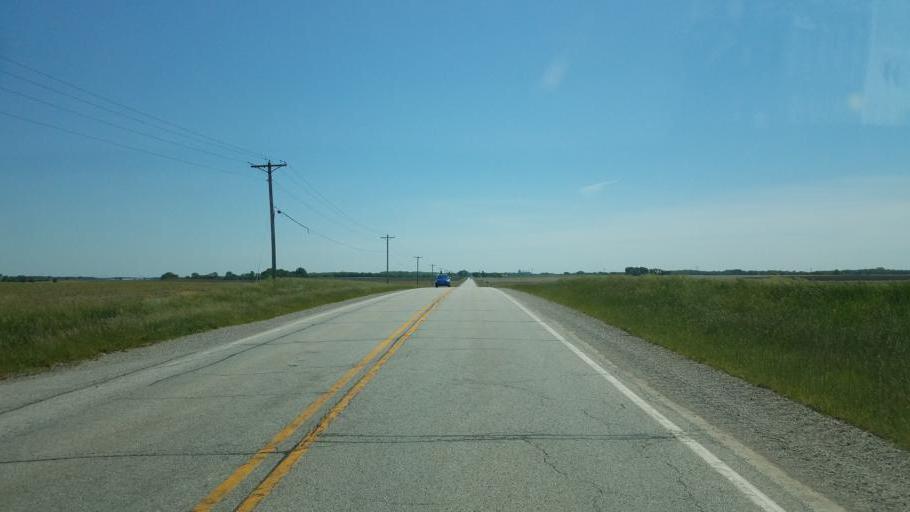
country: US
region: Illinois
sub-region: McLean County
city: Heyworth
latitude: 40.3120
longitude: -89.0554
